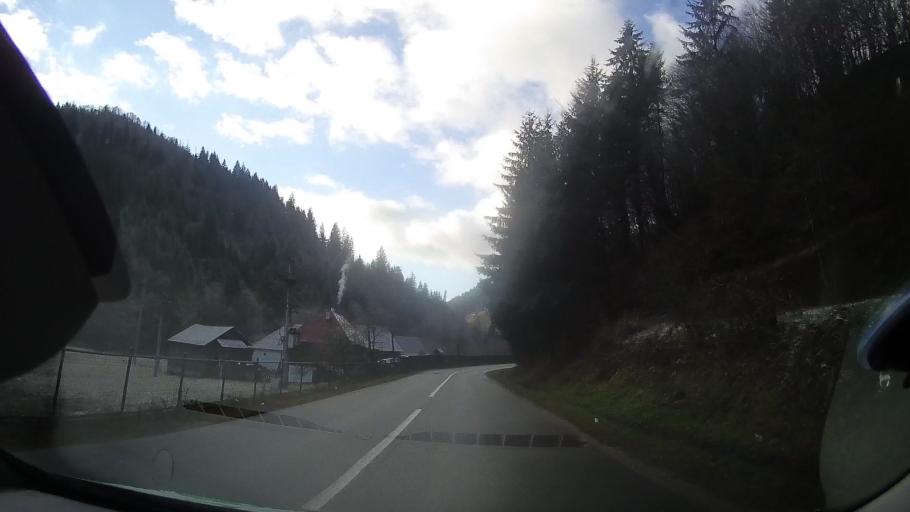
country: RO
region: Alba
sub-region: Comuna Vadu Motilor
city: Vadu Motilor
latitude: 46.4138
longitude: 22.9688
